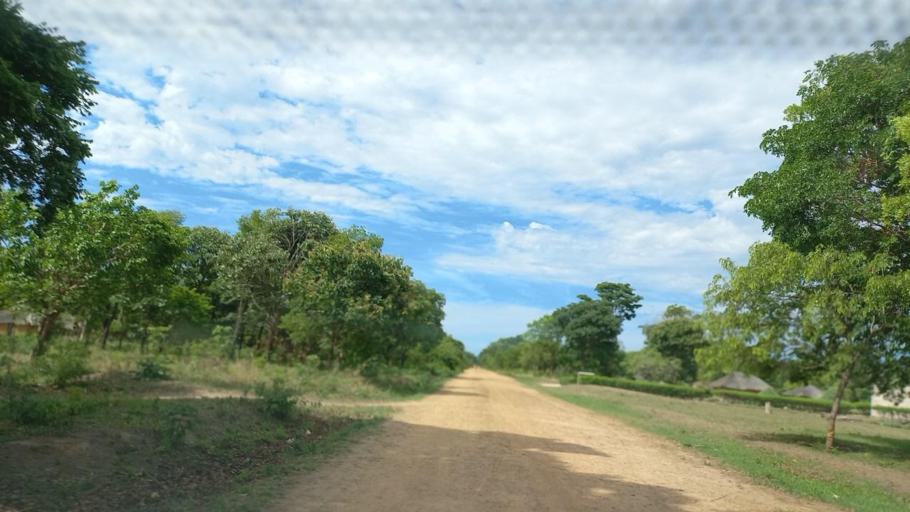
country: ZM
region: North-Western
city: Kabompo
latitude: -13.5225
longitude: 24.3831
